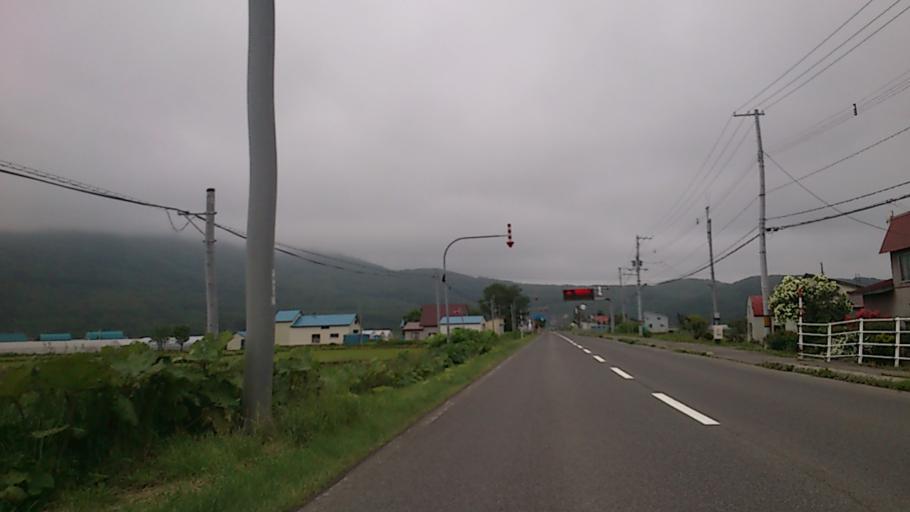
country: JP
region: Hokkaido
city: Iwanai
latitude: 42.7993
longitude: 140.4925
